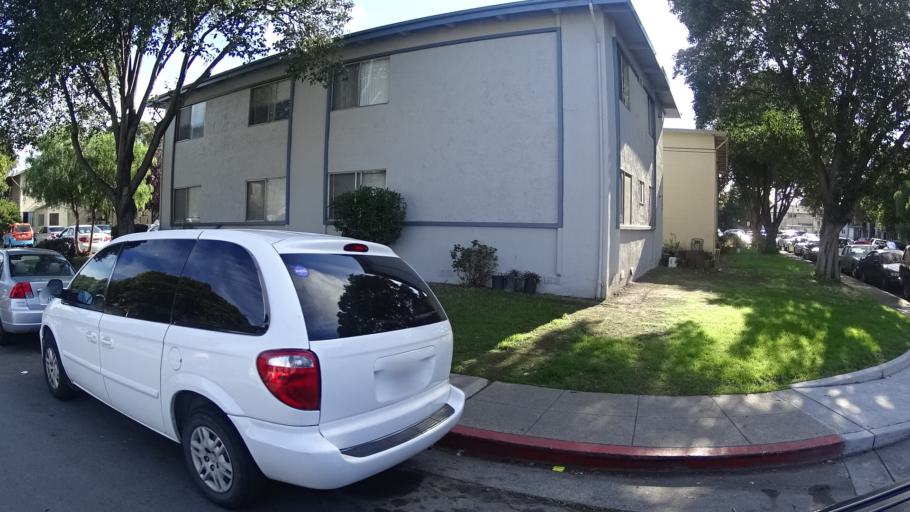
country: US
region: California
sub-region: Santa Clara County
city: Santa Clara
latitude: 37.3645
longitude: -121.9634
